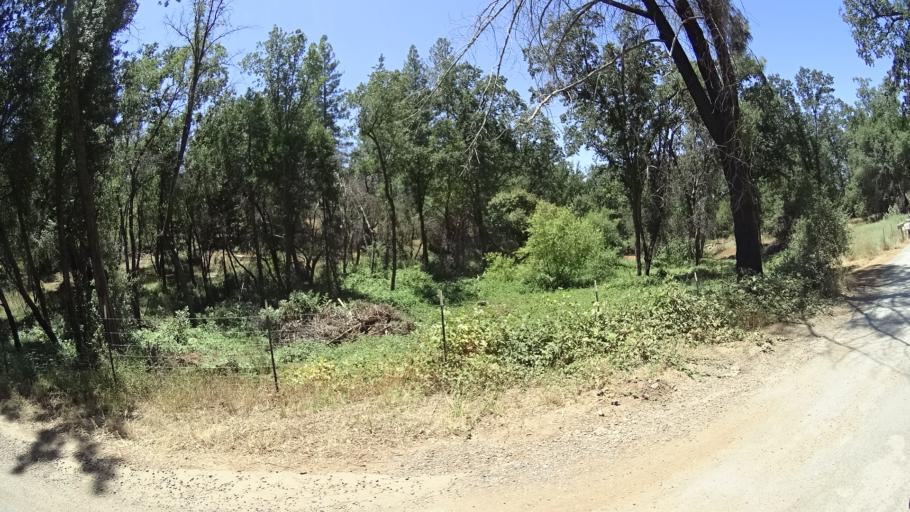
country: US
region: California
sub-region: Calaveras County
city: Mountain Ranch
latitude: 38.2472
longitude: -120.5839
